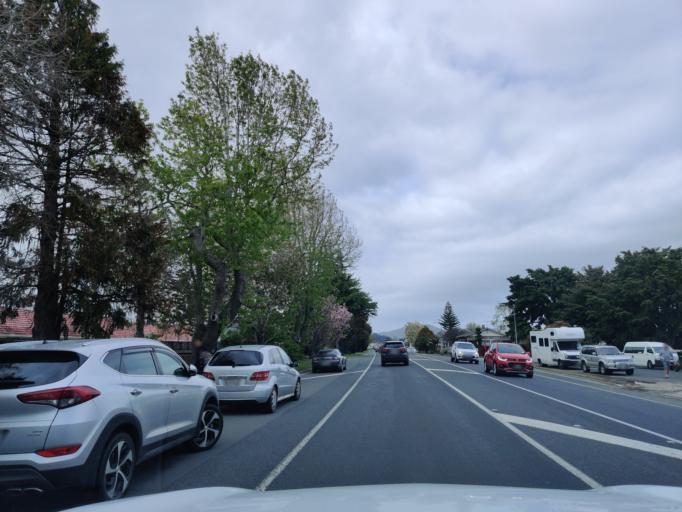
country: NZ
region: Waikato
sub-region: Waikato District
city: Ngaruawahia
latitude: -37.5491
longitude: 175.1585
